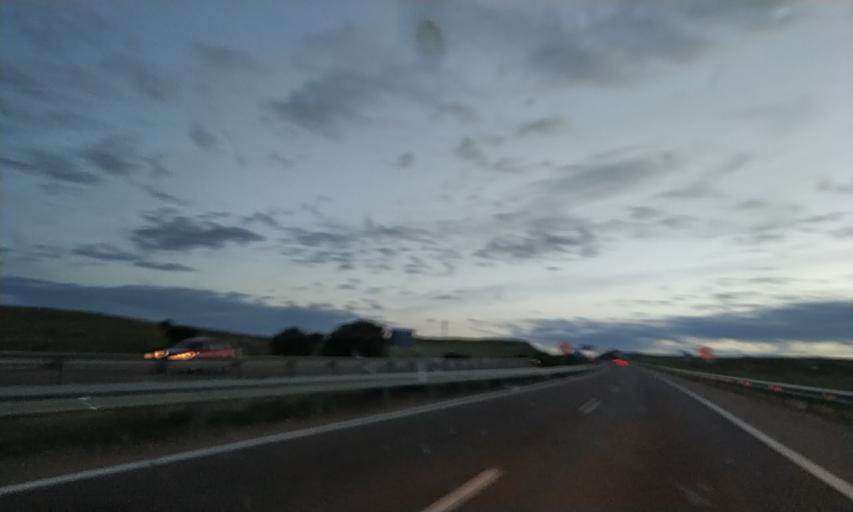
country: ES
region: Extremadura
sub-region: Provincia de Badajoz
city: Badajoz
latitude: 38.9139
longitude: -6.9880
